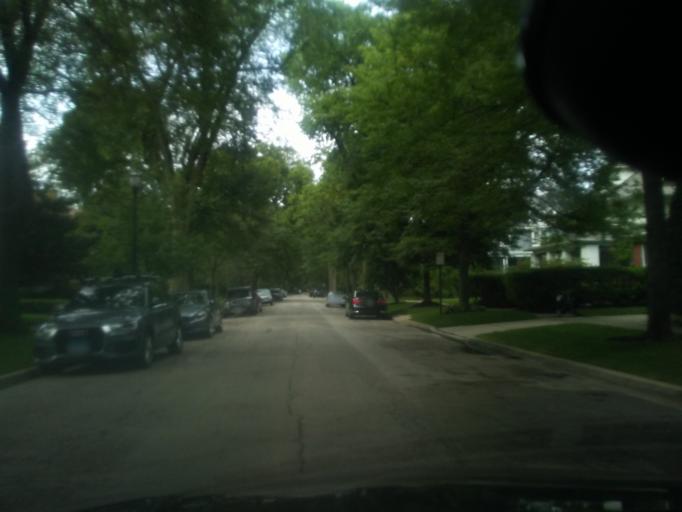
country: US
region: Illinois
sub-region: Cook County
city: Evanston
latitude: 42.0361
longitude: -87.6736
